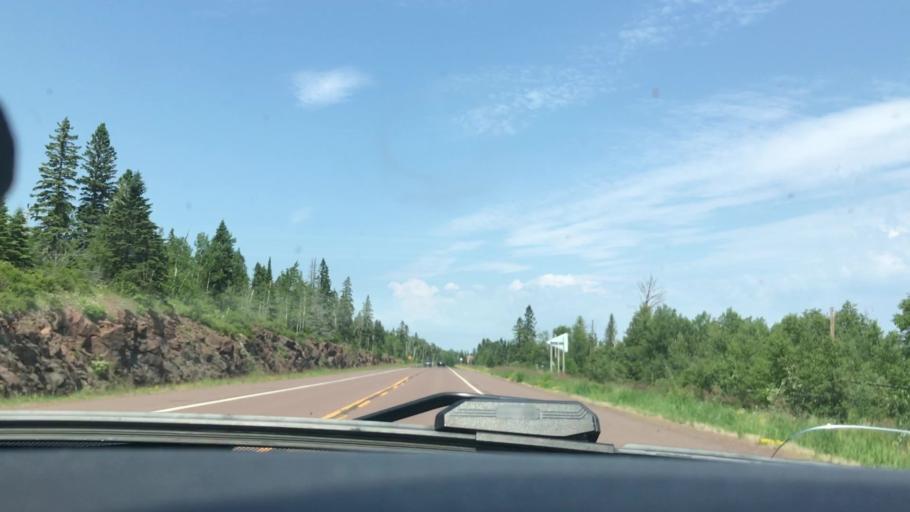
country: US
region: Minnesota
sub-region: Cook County
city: Grand Marais
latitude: 47.6153
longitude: -90.7579
